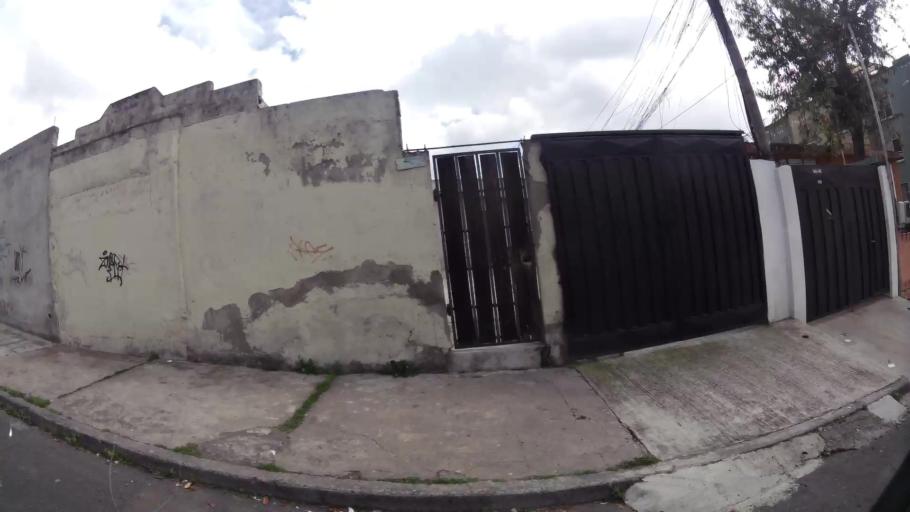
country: EC
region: Pichincha
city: Quito
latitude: -0.1463
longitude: -78.4954
